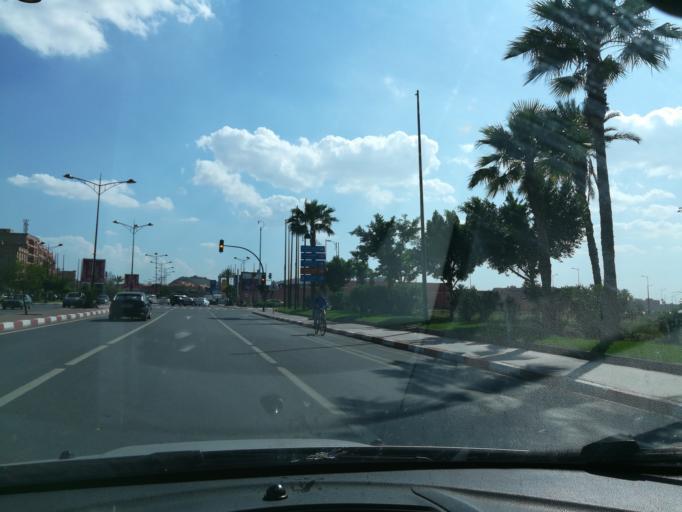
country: MA
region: Marrakech-Tensift-Al Haouz
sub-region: Marrakech
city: Marrakesh
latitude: 31.6590
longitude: -8.0168
